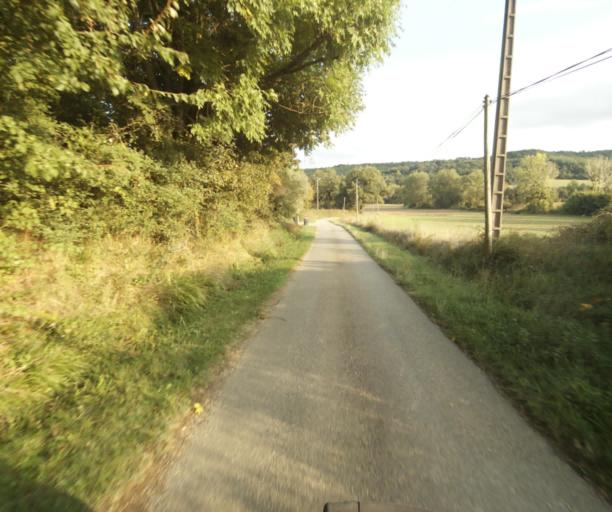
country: FR
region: Midi-Pyrenees
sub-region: Departement de la Haute-Garonne
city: Launac
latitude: 43.8191
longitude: 1.1223
